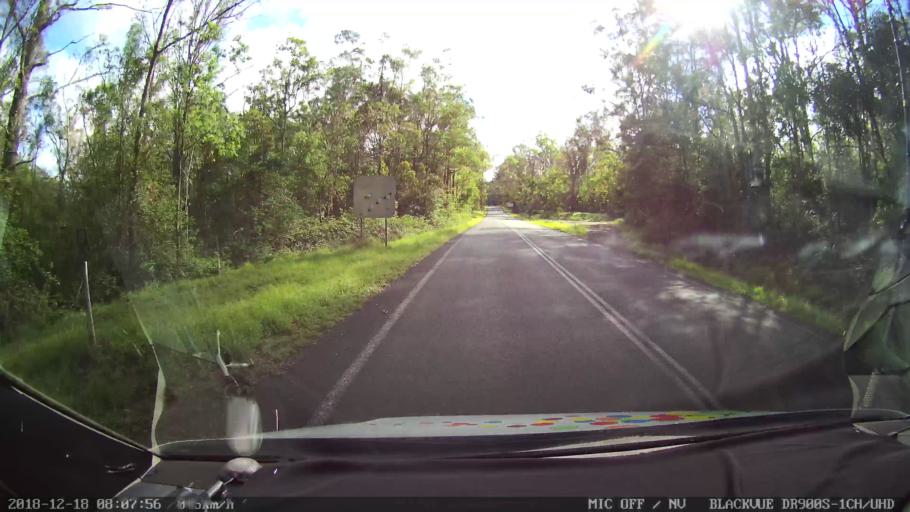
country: AU
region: New South Wales
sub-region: Kyogle
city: Kyogle
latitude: -28.3831
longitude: 152.6464
